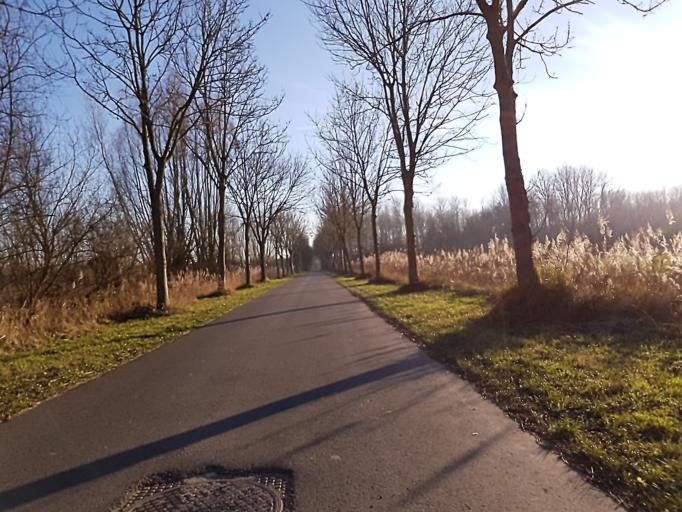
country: BE
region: Flanders
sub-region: Provincie Antwerpen
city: Puurs
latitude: 51.1112
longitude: 4.2860
